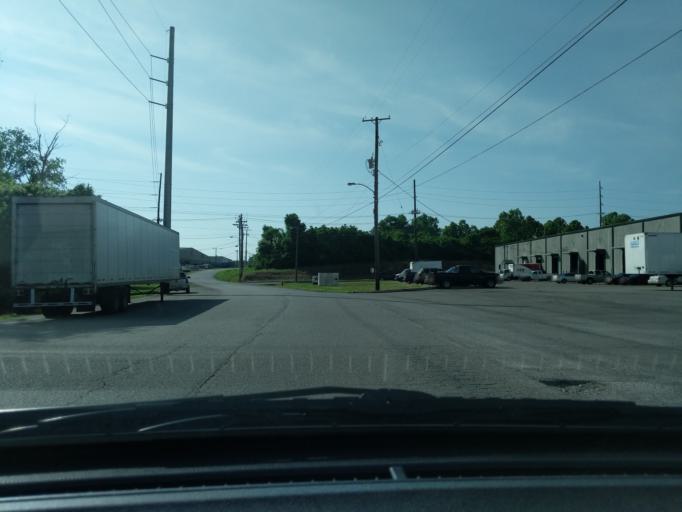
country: US
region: Tennessee
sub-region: Davidson County
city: Oak Hill
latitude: 36.0948
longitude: -86.6960
